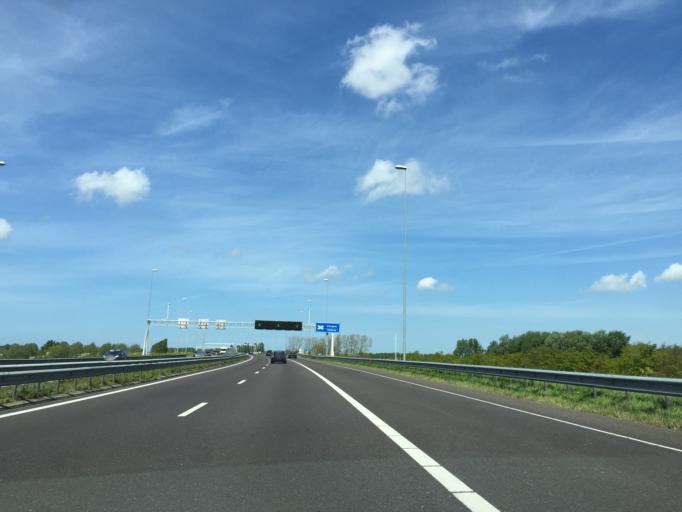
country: NL
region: North Holland
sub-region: Gemeente Velsen
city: Velsen-Zuid
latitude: 52.4170
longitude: 4.6970
